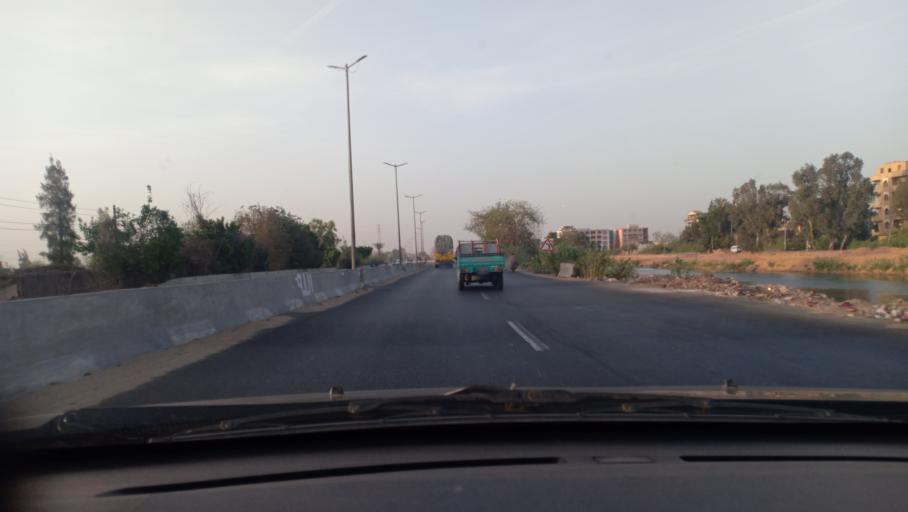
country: EG
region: Muhafazat al Minufiyah
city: Quwaysina
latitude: 30.5609
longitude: 31.2691
